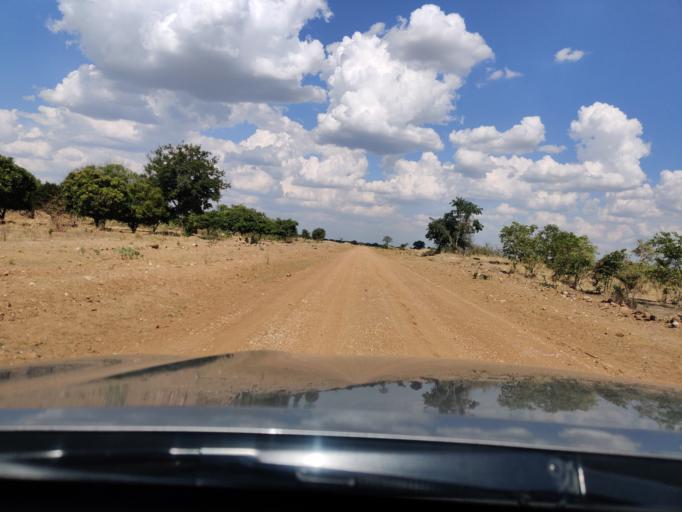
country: ZM
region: Central
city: Chibombo
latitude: -14.7592
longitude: 27.8745
